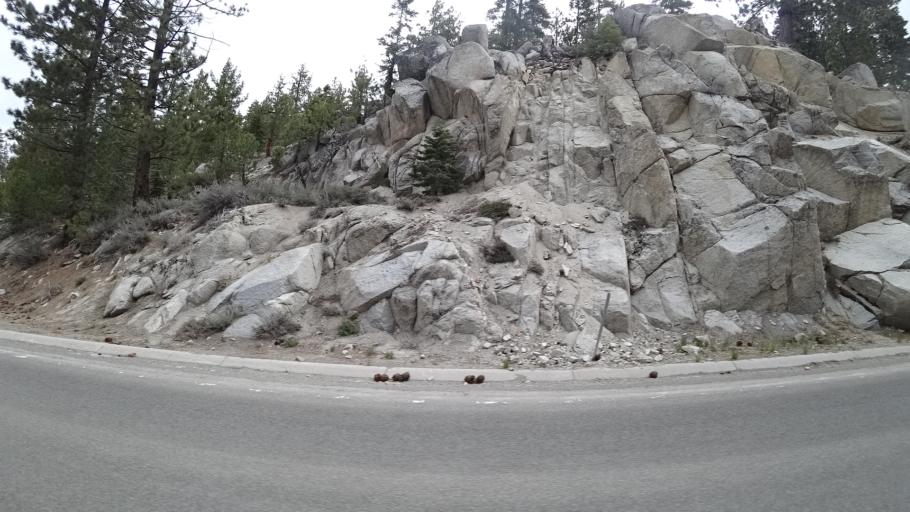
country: US
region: Nevada
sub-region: Washoe County
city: Incline Village
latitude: 39.1418
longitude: -119.9255
